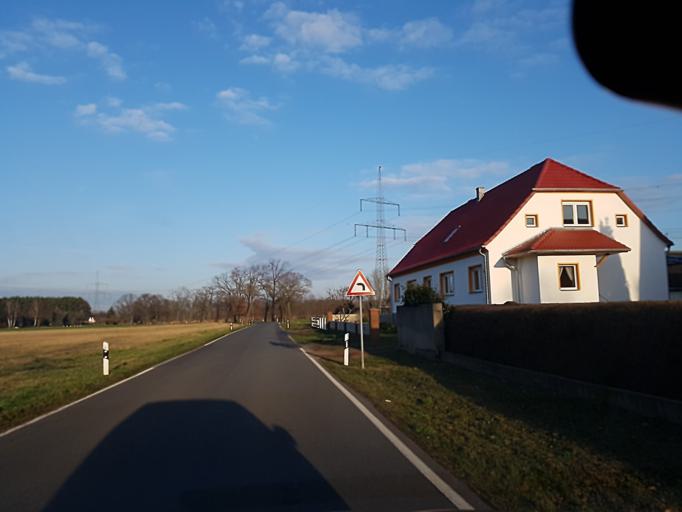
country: DE
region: Brandenburg
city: Bad Liebenwerda
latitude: 51.5308
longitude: 13.4233
